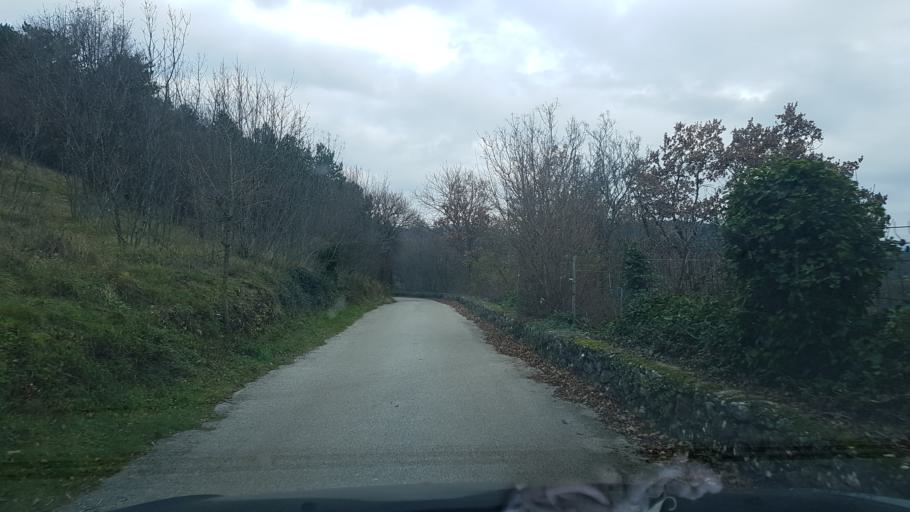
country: IT
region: Friuli Venezia Giulia
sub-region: Provincia di Trieste
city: Zolla
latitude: 45.7201
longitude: 13.8023
